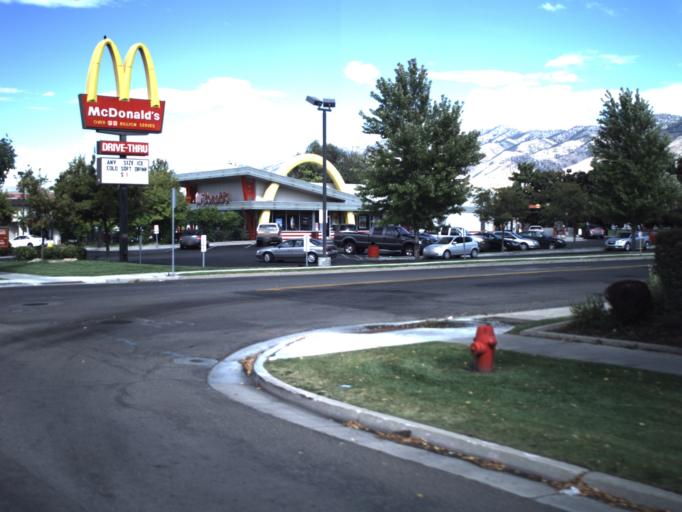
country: US
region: Utah
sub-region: Cache County
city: Logan
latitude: 41.7461
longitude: -111.8345
